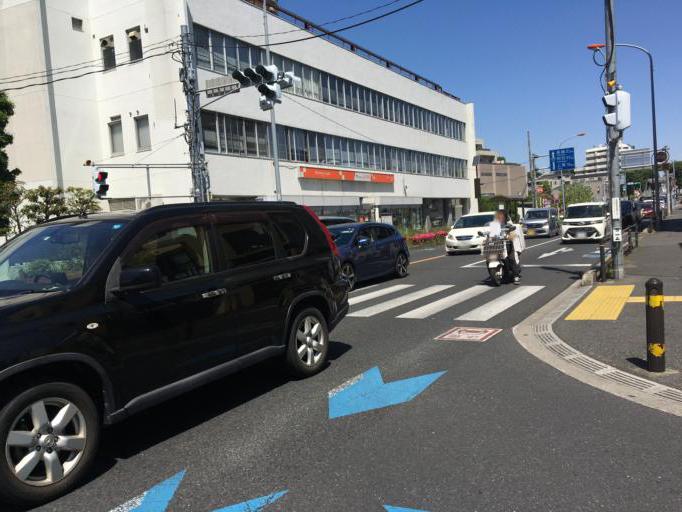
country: JP
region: Saitama
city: Yono
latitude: 35.8465
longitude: 139.6509
